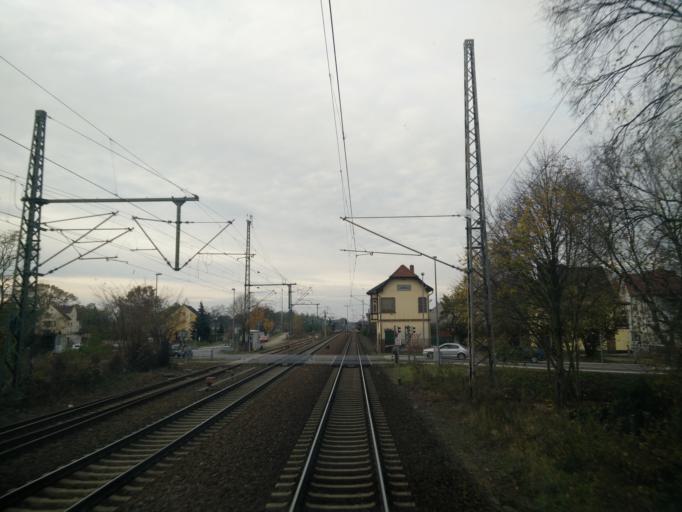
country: DE
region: Brandenburg
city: Luebben
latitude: 51.9376
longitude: 13.8807
